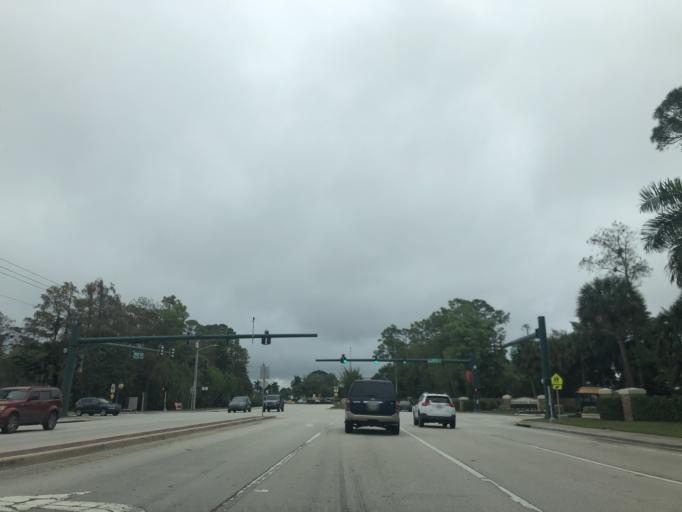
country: US
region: Florida
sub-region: Palm Beach County
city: Wellington
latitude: 26.6783
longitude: -80.2480
